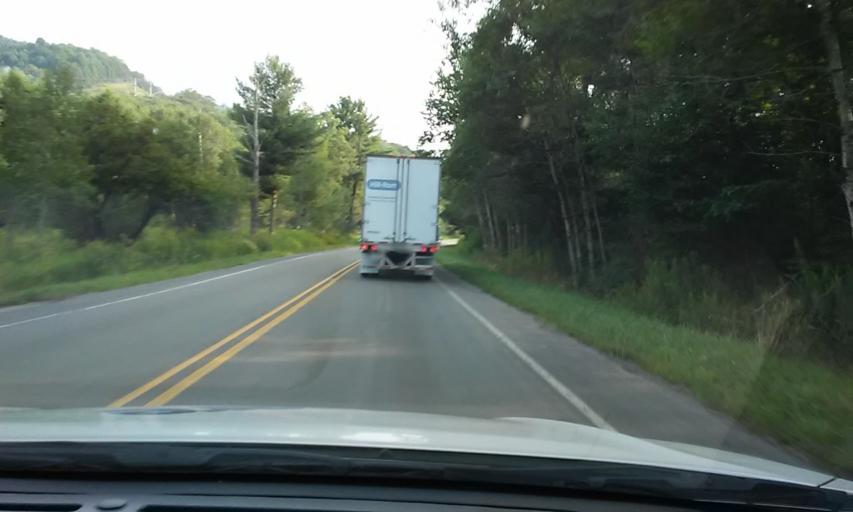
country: US
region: Pennsylvania
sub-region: McKean County
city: Smethport
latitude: 41.7475
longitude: -78.5276
